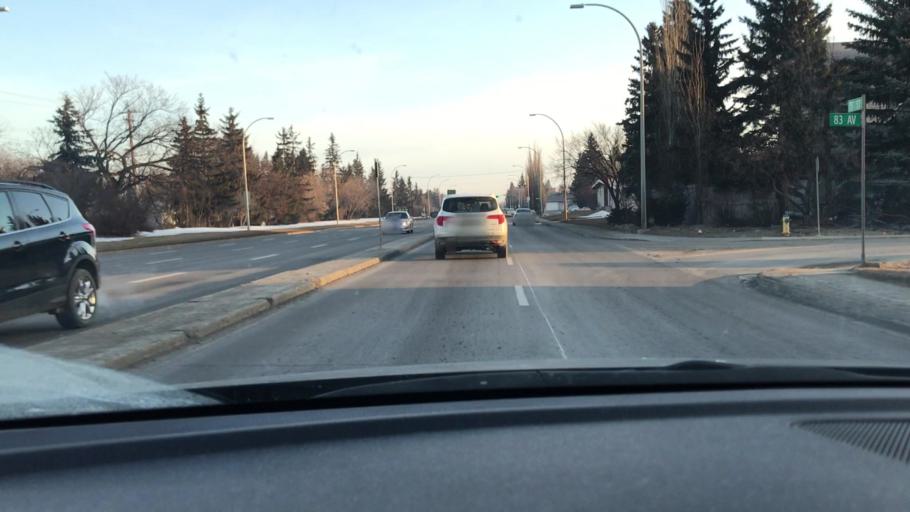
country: CA
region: Alberta
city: Edmonton
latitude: 53.5188
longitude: -113.4428
